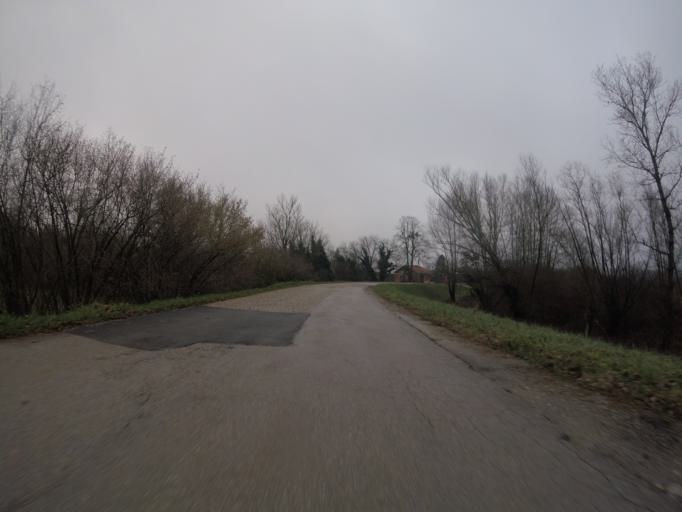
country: HR
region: Zagrebacka
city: Kuce
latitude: 45.7082
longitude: 16.2181
